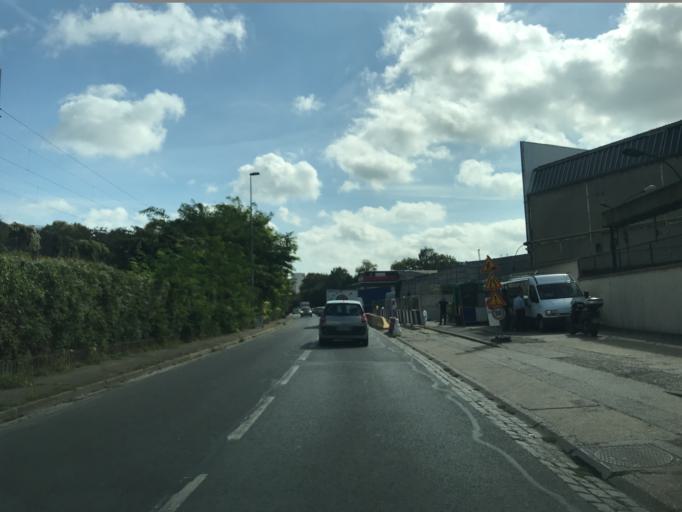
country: FR
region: Ile-de-France
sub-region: Departement de Seine-Saint-Denis
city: Bobigny
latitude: 48.9057
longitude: 2.4347
